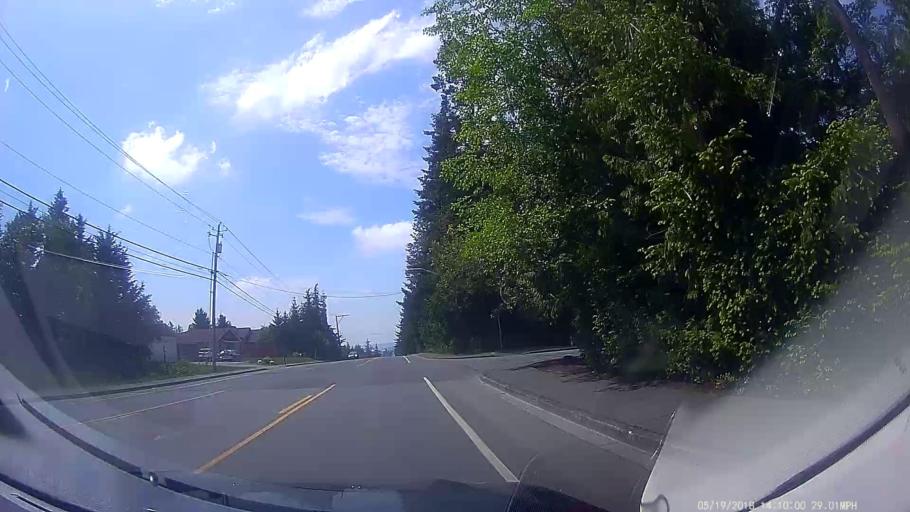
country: US
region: Washington
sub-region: Skagit County
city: Mount Vernon
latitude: 48.4210
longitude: -122.2895
